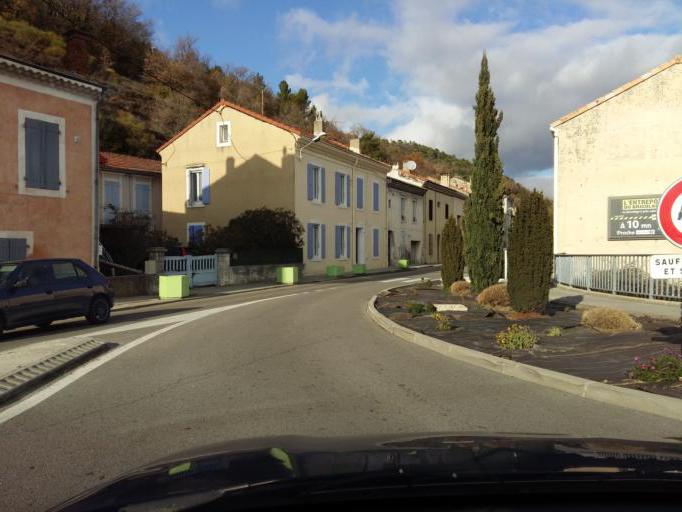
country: FR
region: Rhone-Alpes
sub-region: Departement de l'Ardeche
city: Le Teil
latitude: 44.5561
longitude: 4.6868
